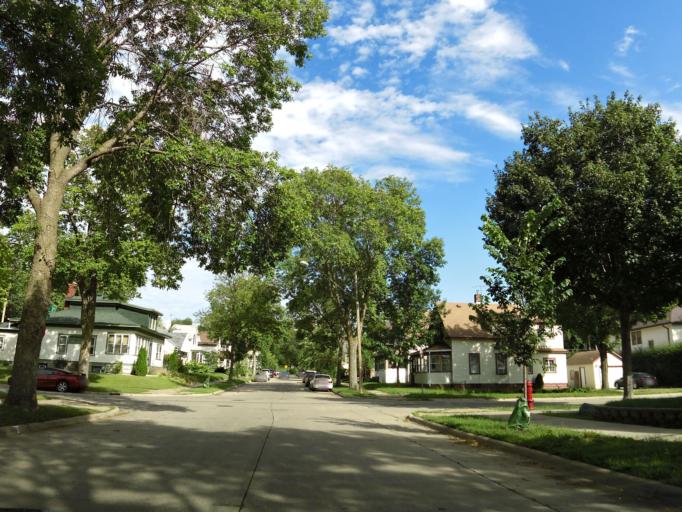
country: US
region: Minnesota
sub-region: Hennepin County
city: Saint Anthony
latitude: 45.0122
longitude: -93.2442
